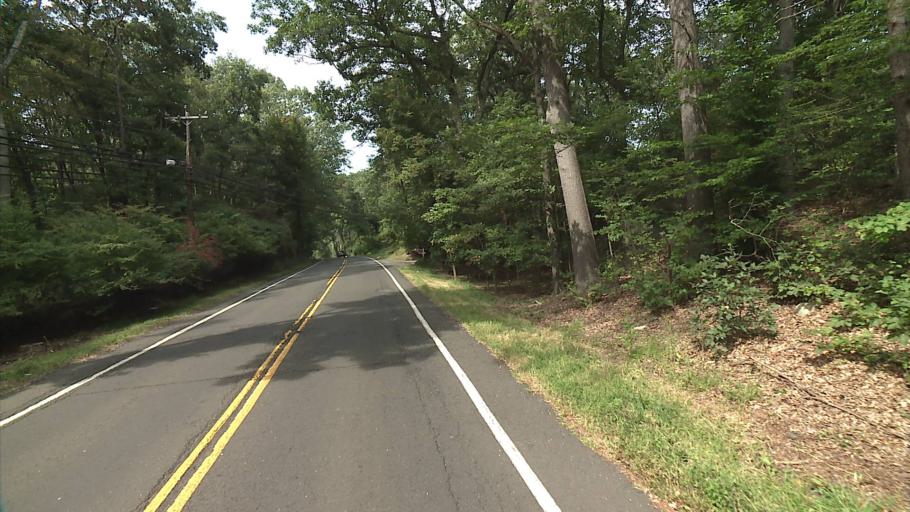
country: US
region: Connecticut
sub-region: Fairfield County
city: North Stamford
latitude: 41.1292
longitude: -73.5807
